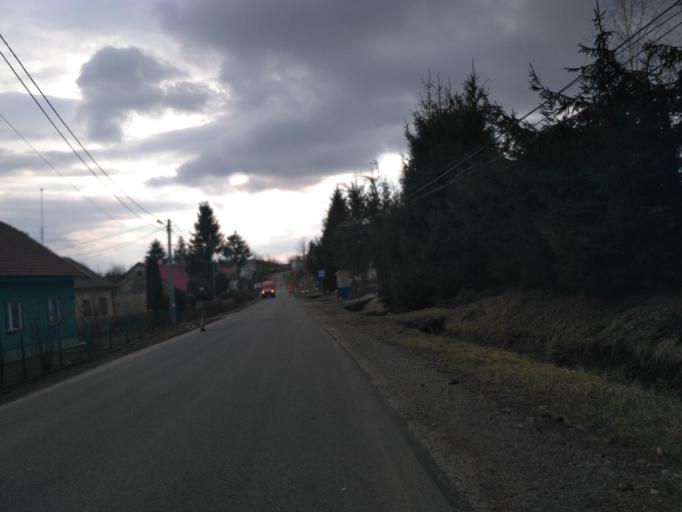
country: PL
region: Subcarpathian Voivodeship
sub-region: Powiat sanocki
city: Strachocina
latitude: 49.6090
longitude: 22.1443
